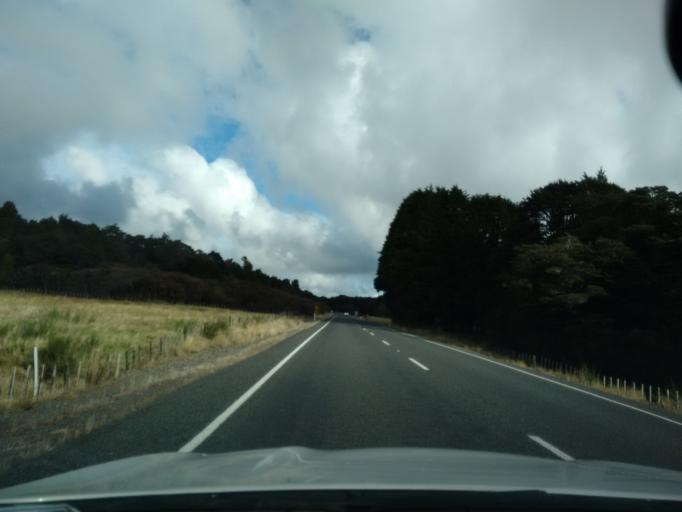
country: NZ
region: Manawatu-Wanganui
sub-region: Ruapehu District
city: Waiouru
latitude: -39.2967
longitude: 175.3880
